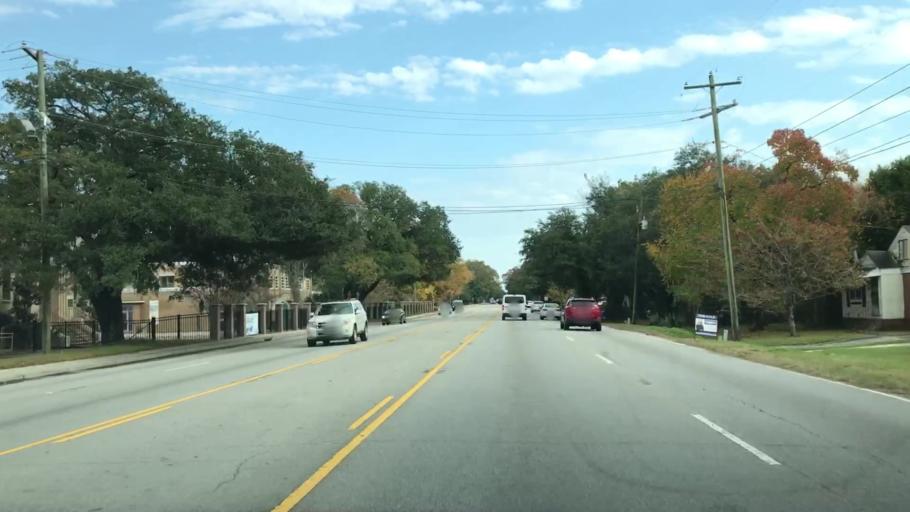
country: US
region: South Carolina
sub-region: Charleston County
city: Charleston
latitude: 32.7815
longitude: -79.9831
